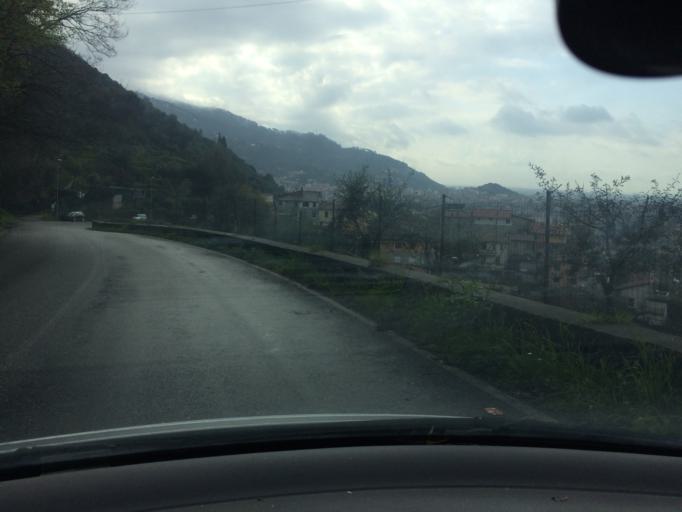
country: IT
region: Tuscany
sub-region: Provincia di Massa-Carrara
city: Massa
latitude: 44.0525
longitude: 10.1256
